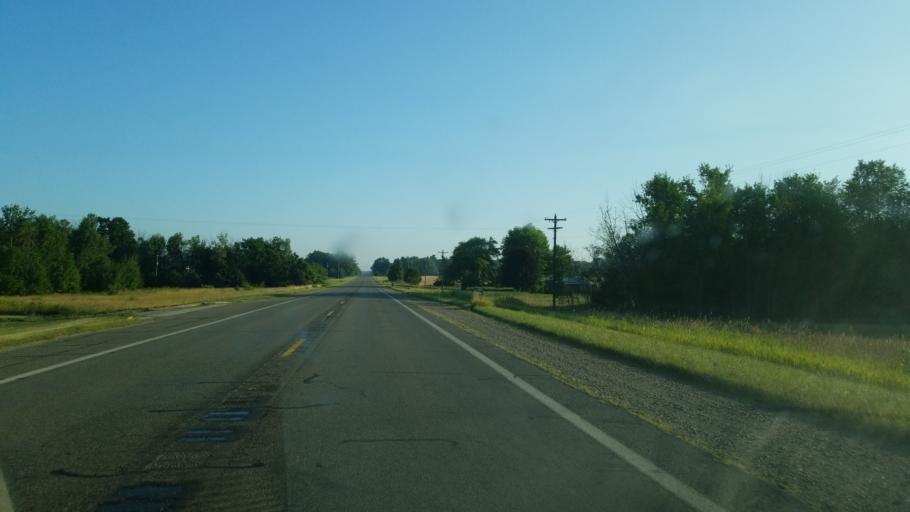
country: US
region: Michigan
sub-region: Montcalm County
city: Edmore
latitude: 43.3876
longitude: -85.0846
